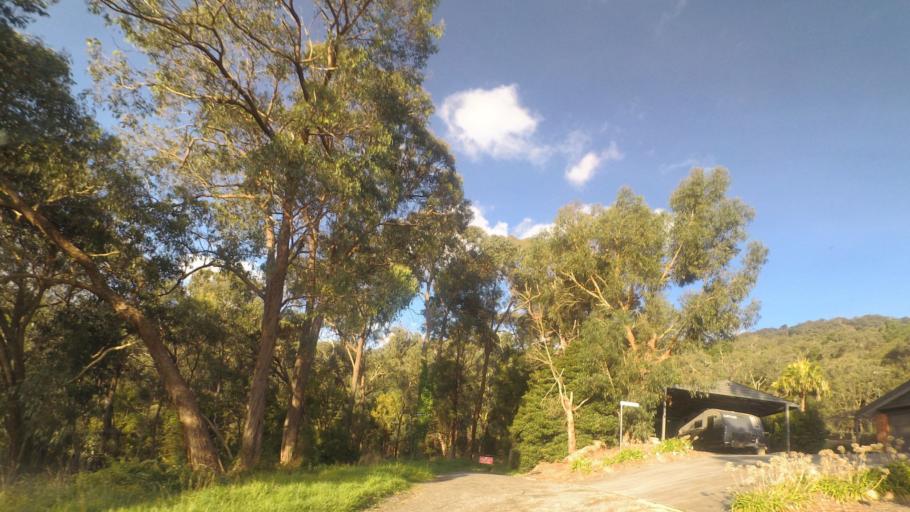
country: AU
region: Victoria
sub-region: Yarra Ranges
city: Kalorama
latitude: -37.8098
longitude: 145.3650
